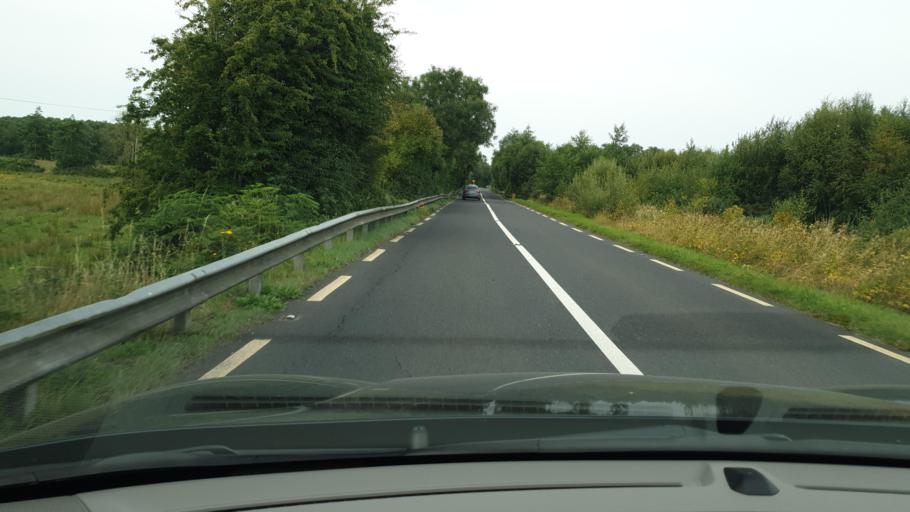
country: IE
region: Leinster
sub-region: An Mhi
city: Trim
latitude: 53.6345
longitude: -6.8165
